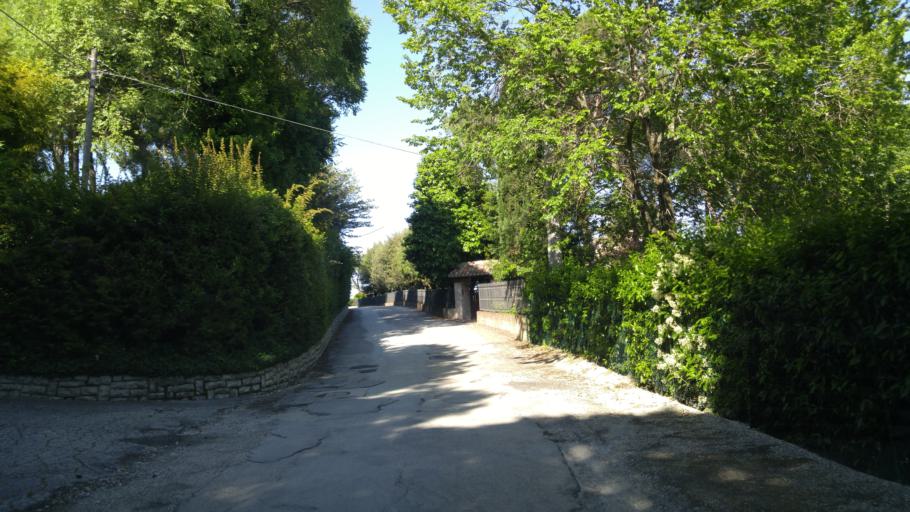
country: IT
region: The Marches
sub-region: Provincia di Pesaro e Urbino
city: Centinarola
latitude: 43.8496
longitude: 12.9936
